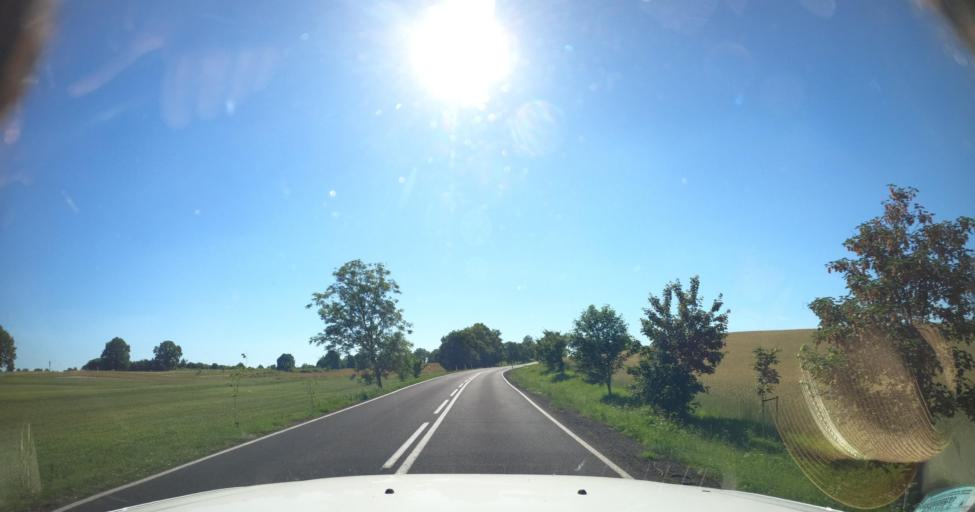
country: PL
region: West Pomeranian Voivodeship
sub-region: Powiat drawski
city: Zlocieniec
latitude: 53.5240
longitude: 15.9334
